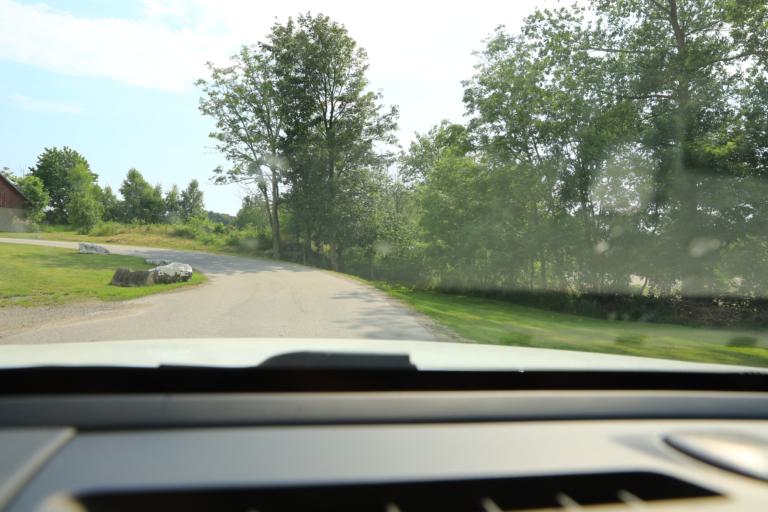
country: SE
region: Halland
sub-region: Varbergs Kommun
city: Varberg
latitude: 57.1583
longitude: 12.3150
